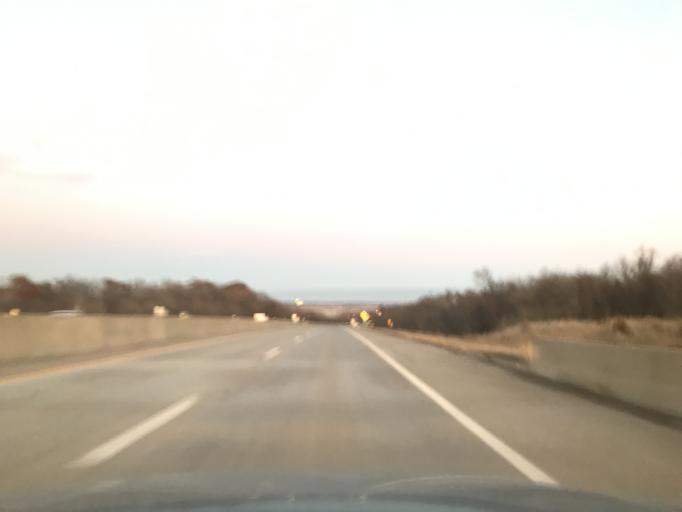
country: US
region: Missouri
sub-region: Marion County
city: Hannibal
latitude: 39.7171
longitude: -91.3726
